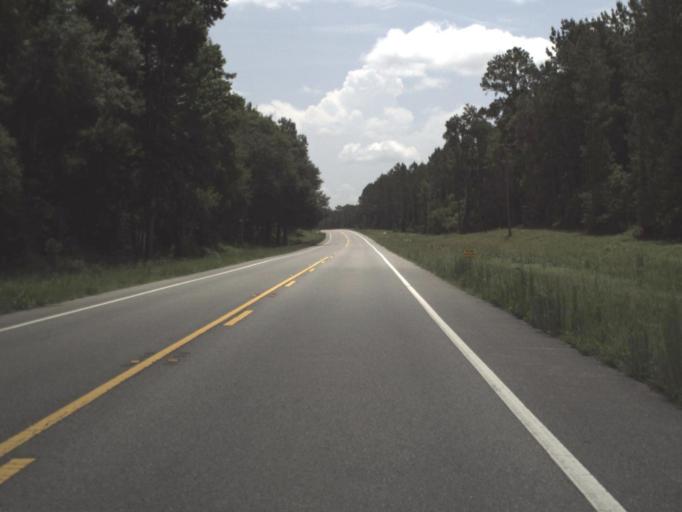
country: US
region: Florida
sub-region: Madison County
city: Madison
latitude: 30.4893
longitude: -83.5041
